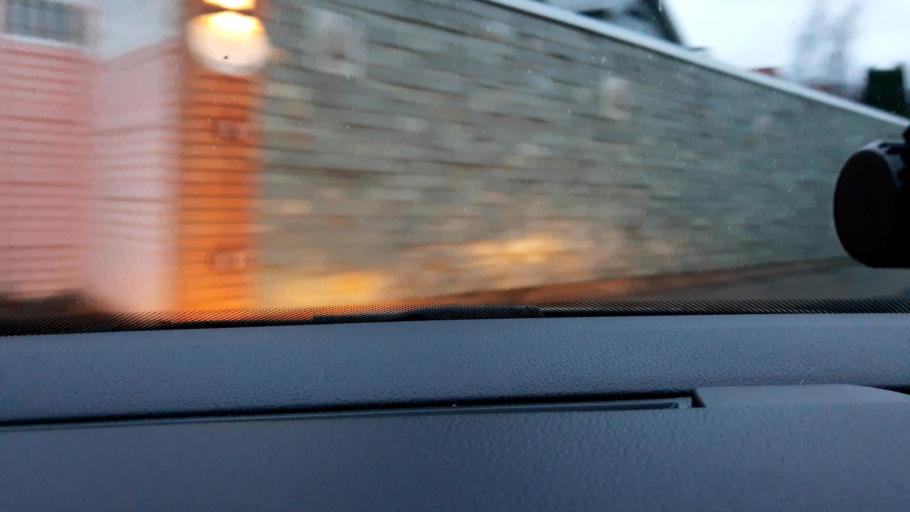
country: RU
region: Moskovskaya
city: Zarech'ye
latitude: 55.6786
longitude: 37.3827
